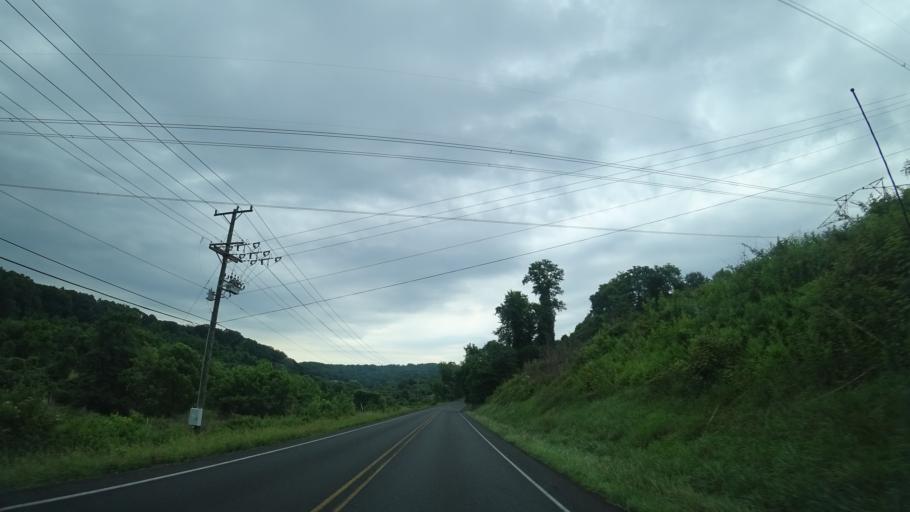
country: US
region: Virginia
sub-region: Warren County
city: Apple Mountain Lake
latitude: 38.9133
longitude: -78.1267
